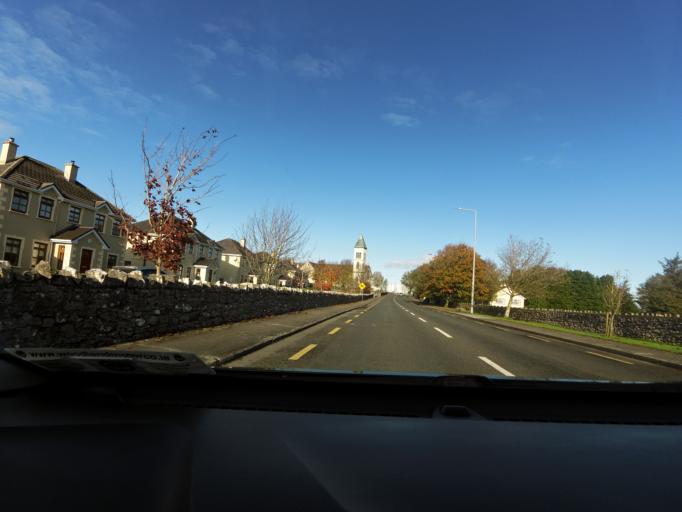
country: IE
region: Connaught
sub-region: Maigh Eo
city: Ballinrobe
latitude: 53.5228
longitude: -9.0904
